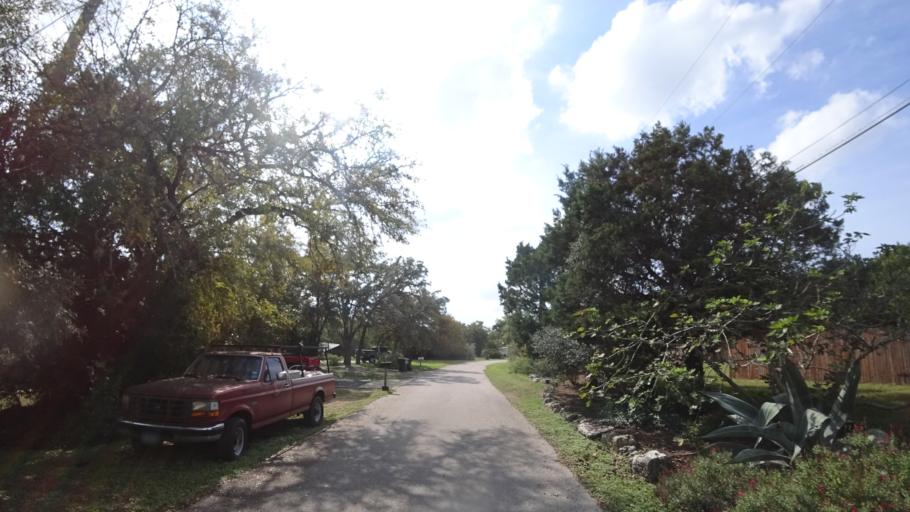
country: US
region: Texas
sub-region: Travis County
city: Hudson Bend
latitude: 30.3844
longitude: -97.9274
